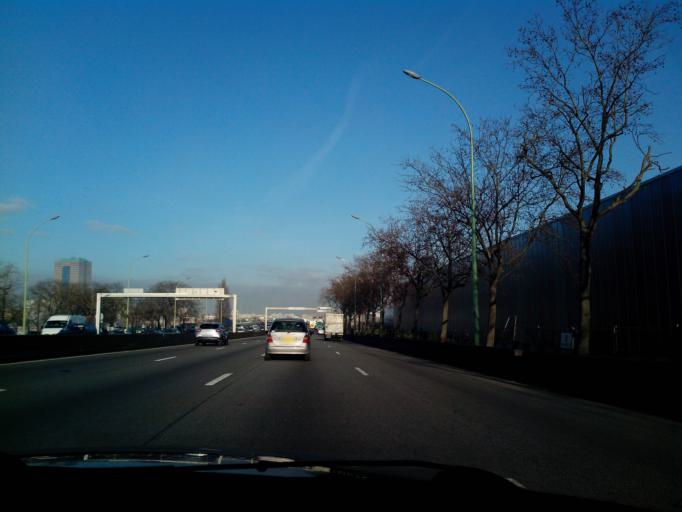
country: FR
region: Ile-de-France
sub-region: Departement de Seine-Saint-Denis
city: Le Pre-Saint-Gervais
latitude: 48.8936
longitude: 2.3953
